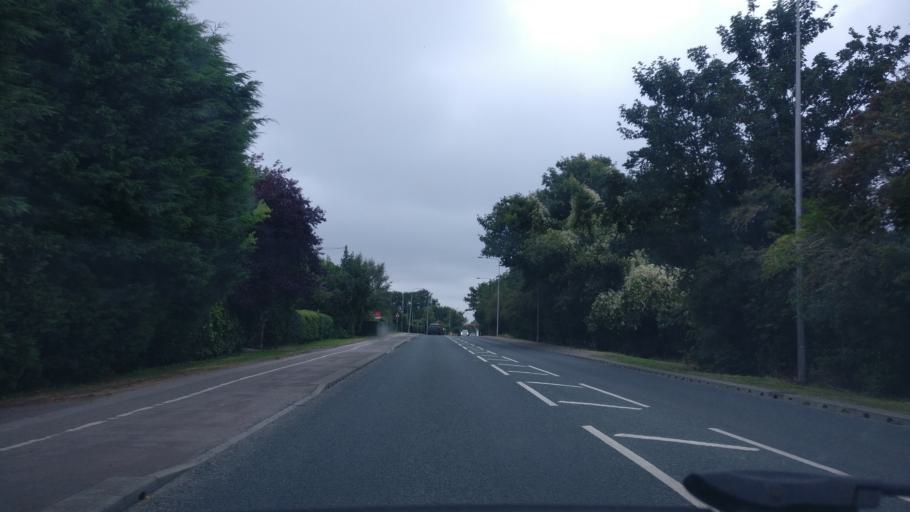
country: GB
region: England
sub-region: East Riding of Yorkshire
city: Beverley
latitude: 53.8258
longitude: -0.4405
